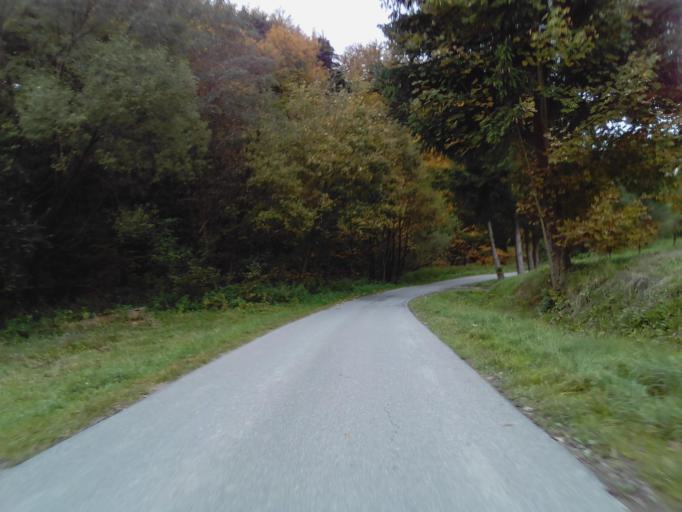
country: PL
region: Subcarpathian Voivodeship
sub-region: Powiat strzyzowski
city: Gwoznica Gorna
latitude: 49.8351
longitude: 21.9964
